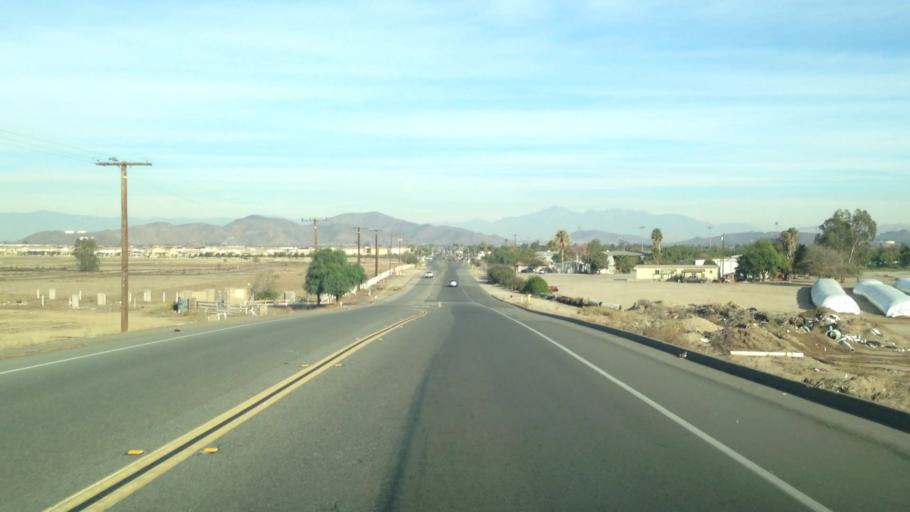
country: US
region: California
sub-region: Riverside County
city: Mira Loma
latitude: 33.9914
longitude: -117.5492
